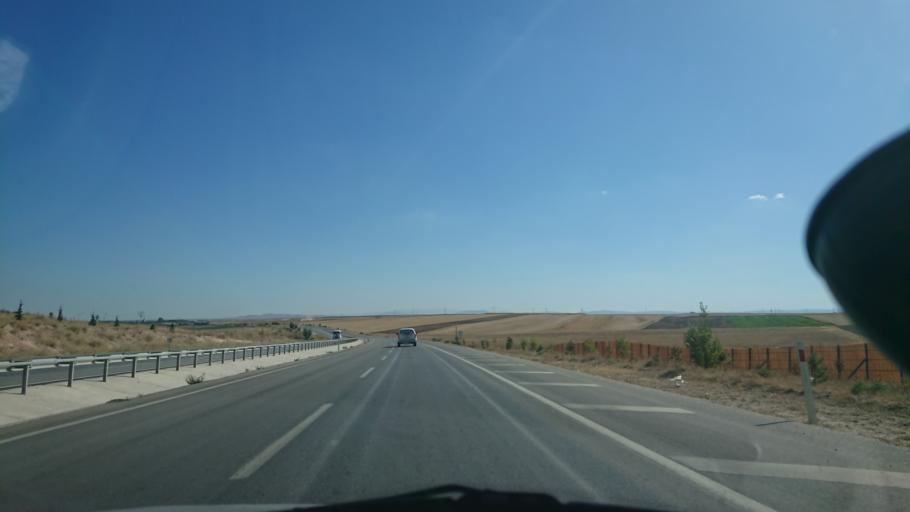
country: TR
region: Eskisehir
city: Mahmudiye
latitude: 39.5041
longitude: 30.9663
